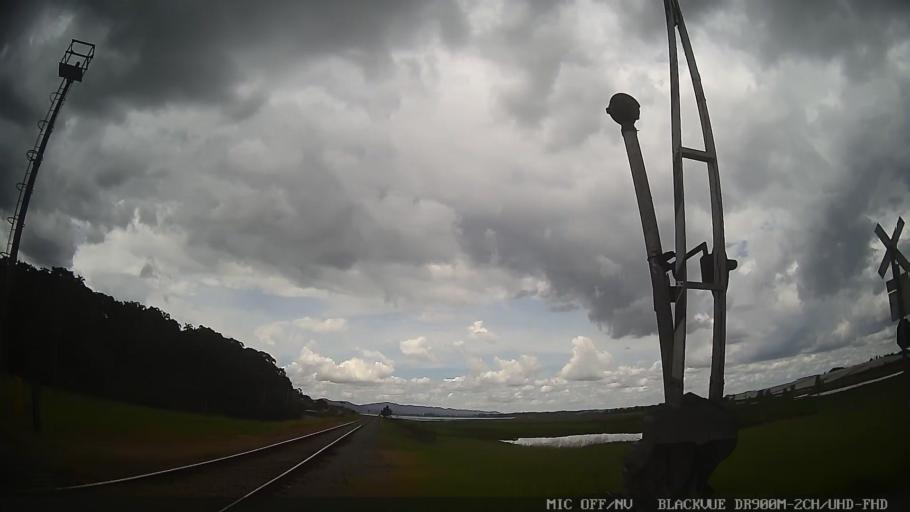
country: BR
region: Sao Paulo
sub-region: Suzano
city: Suzano
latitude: -23.6100
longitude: -46.2992
